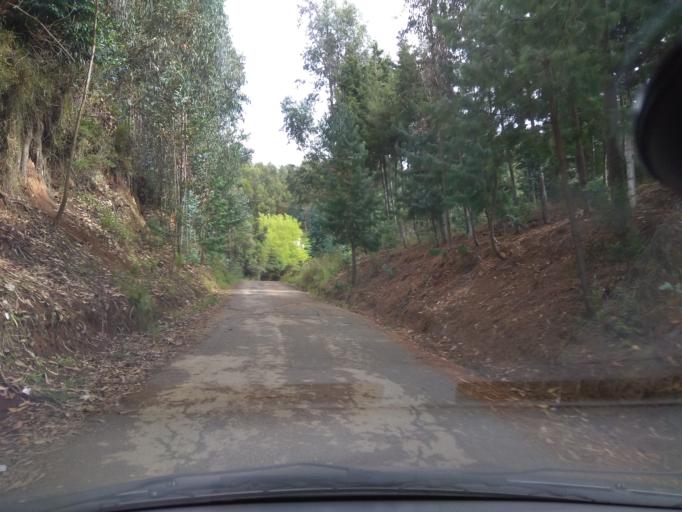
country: CO
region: Boyaca
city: Santa Rosa de Viterbo
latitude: 5.8894
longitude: -72.9749
